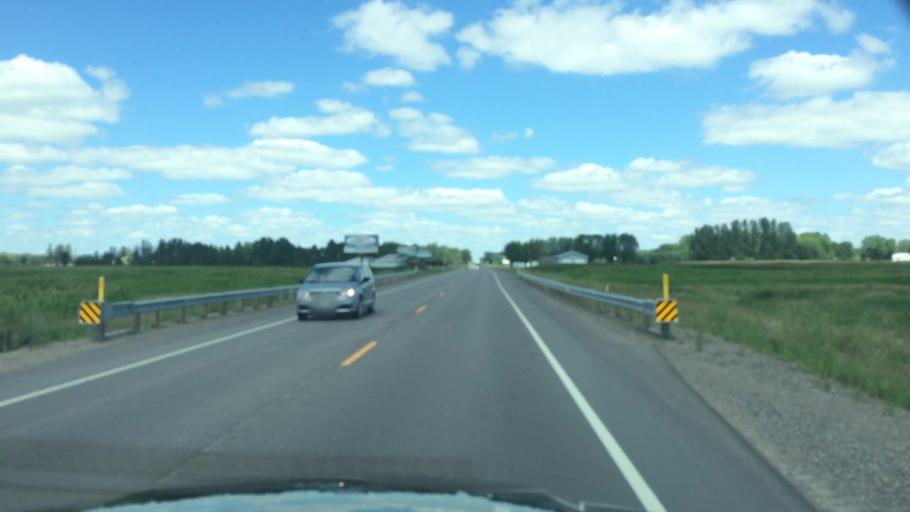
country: US
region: Wisconsin
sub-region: Clark County
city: Abbotsford
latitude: 45.0129
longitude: -90.3153
